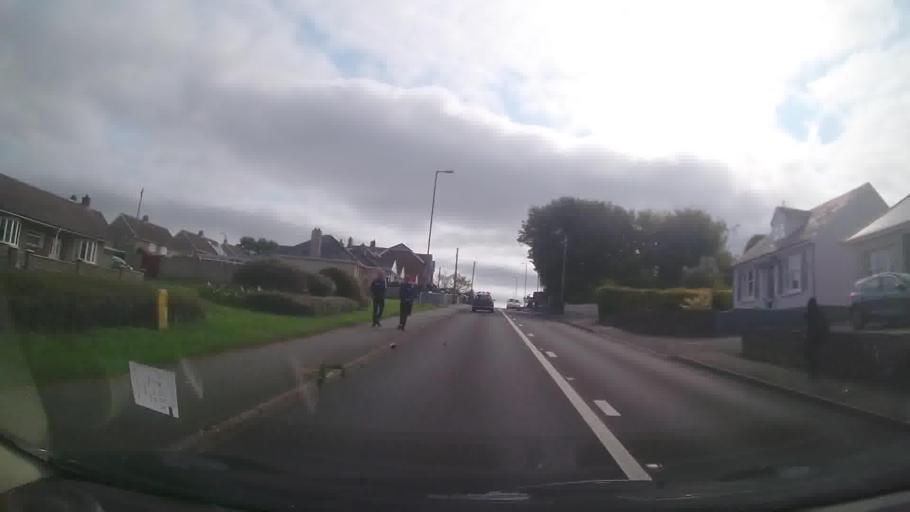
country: GB
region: Wales
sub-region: Pembrokeshire
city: Steynton
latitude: 51.7207
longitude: -5.0242
